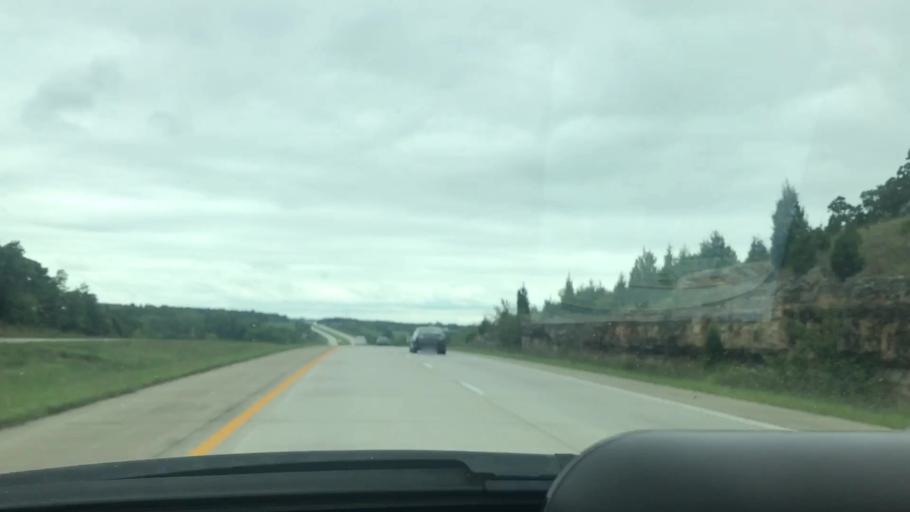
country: US
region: Missouri
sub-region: Dallas County
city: Buffalo
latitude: 37.5221
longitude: -93.1379
